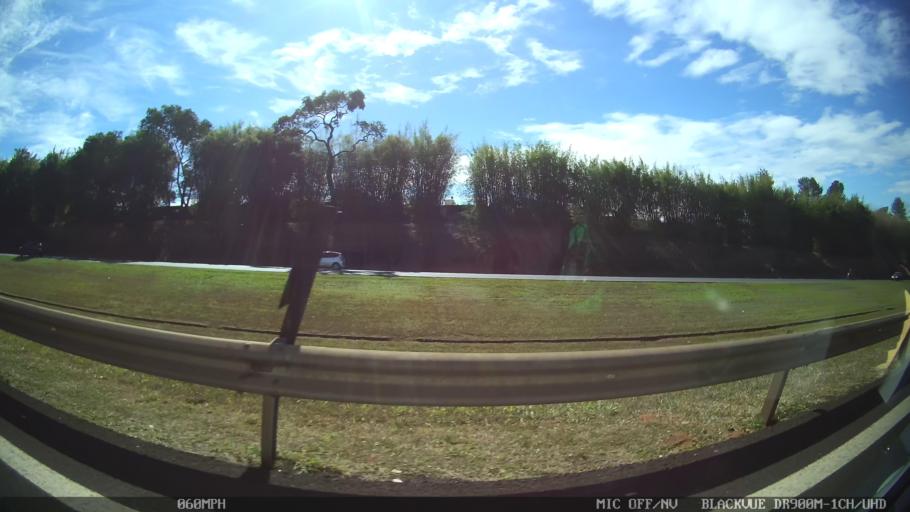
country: BR
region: Sao Paulo
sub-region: Sao Jose Do Rio Preto
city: Sao Jose do Rio Preto
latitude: -20.8170
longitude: -49.4386
